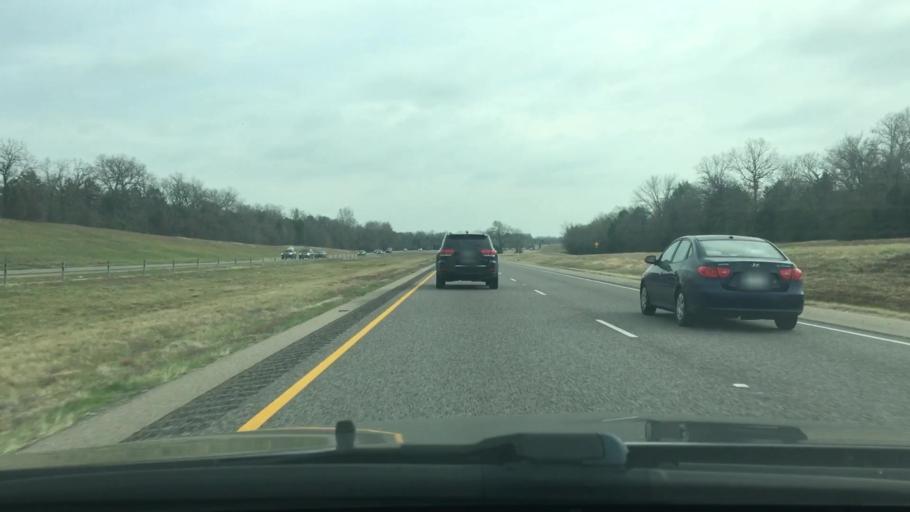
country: US
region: Texas
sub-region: Leon County
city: Buffalo
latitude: 31.5075
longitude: -96.1013
